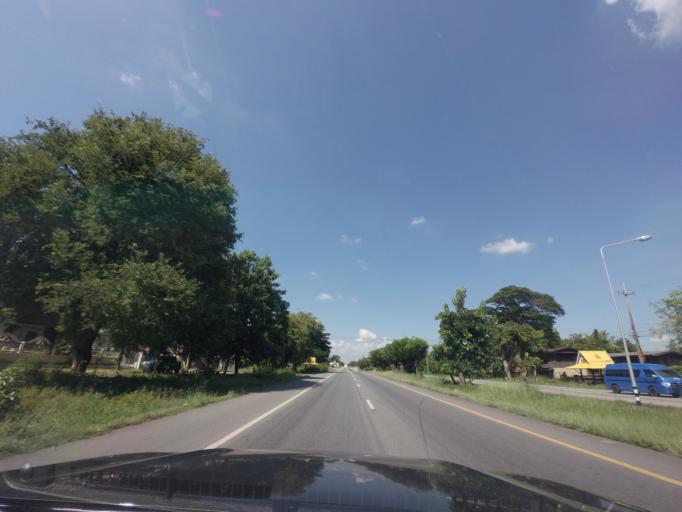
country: TH
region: Nakhon Ratchasima
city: Non Sung
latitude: 15.1503
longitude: 102.3261
